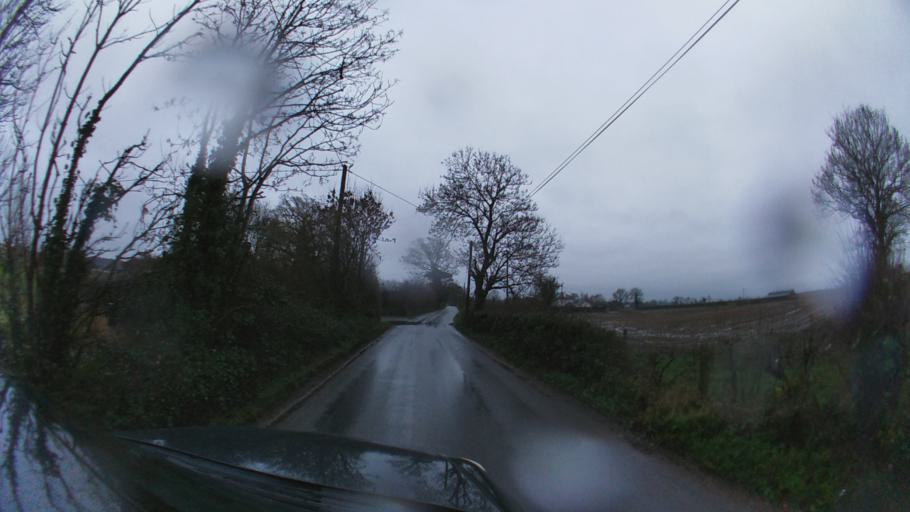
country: IE
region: Leinster
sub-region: County Carlow
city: Bagenalstown
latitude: 52.6678
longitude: -7.0014
